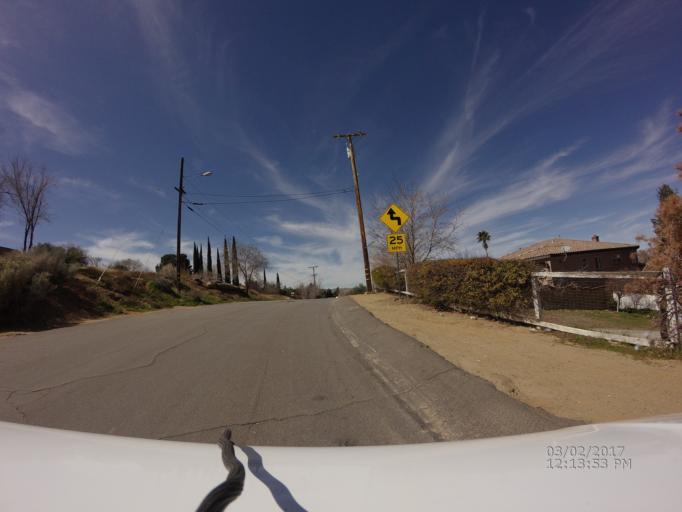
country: US
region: California
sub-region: Los Angeles County
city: Quartz Hill
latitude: 34.6475
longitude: -118.2145
